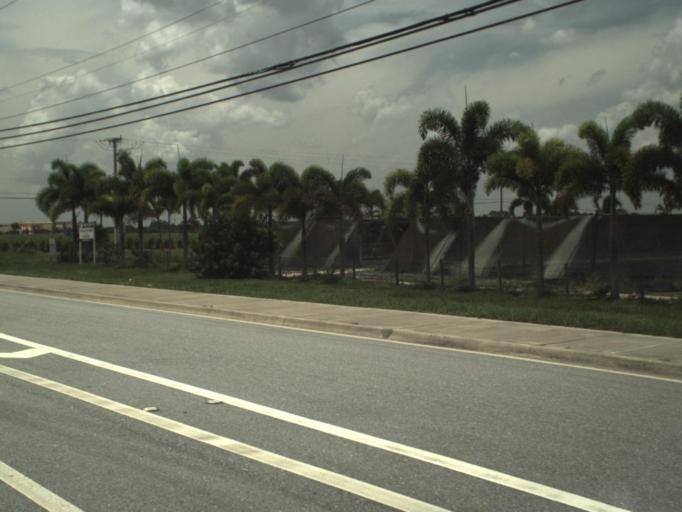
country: US
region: Florida
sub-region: Palm Beach County
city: Villages of Oriole
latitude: 26.4539
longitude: -80.1784
